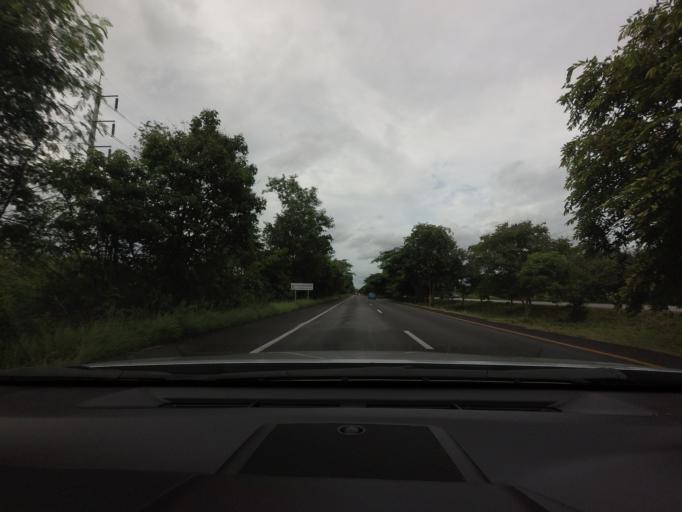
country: TH
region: Prachuap Khiri Khan
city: Hua Hin
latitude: 12.6508
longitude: 99.8698
